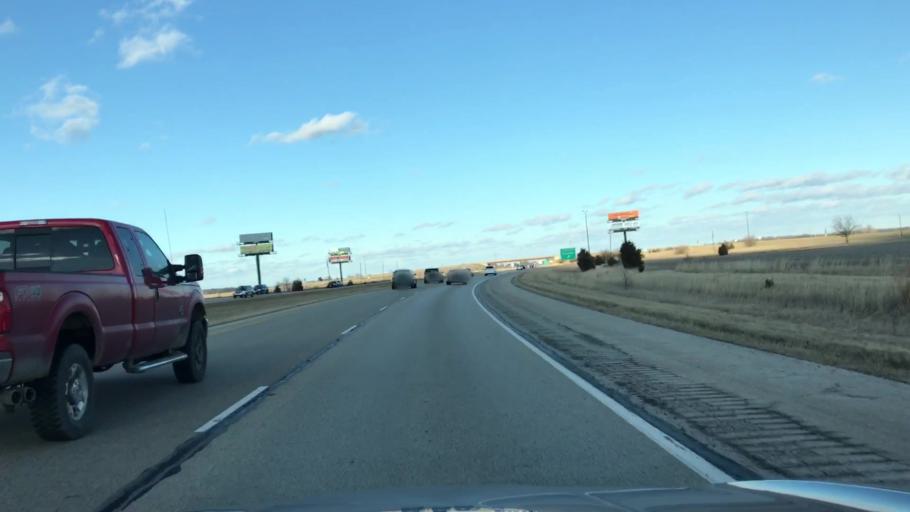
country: US
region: Illinois
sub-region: McLean County
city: Hudson
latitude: 40.5664
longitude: -88.9067
